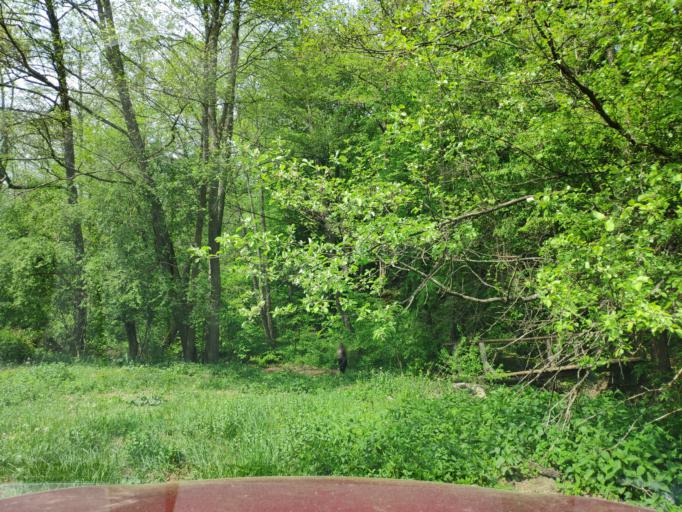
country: SK
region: Banskobystricky
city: Rimavska Sobota
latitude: 48.4867
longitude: 20.0640
